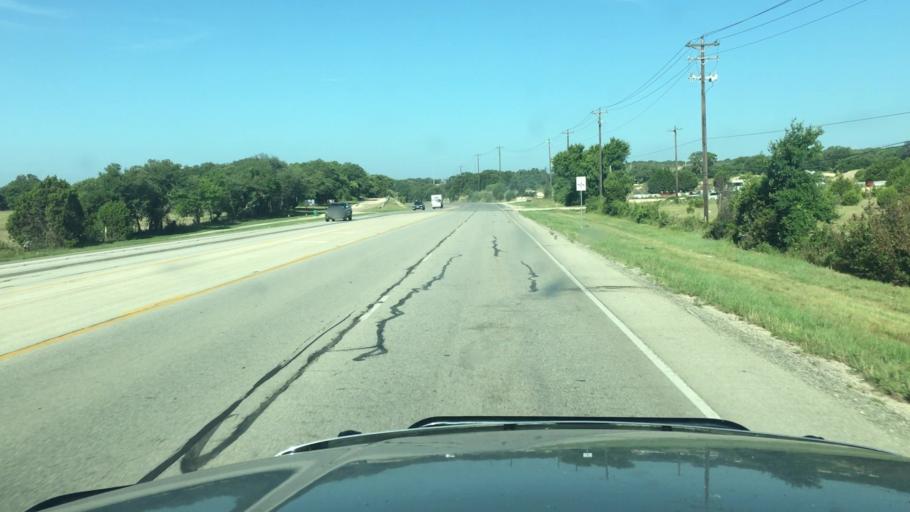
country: US
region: Texas
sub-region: Hays County
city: Dripping Springs
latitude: 30.2059
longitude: -98.1464
